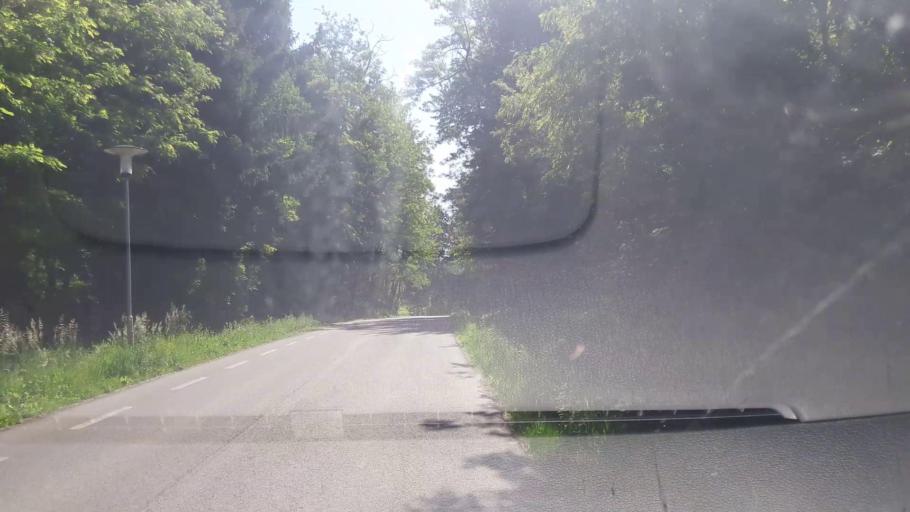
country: AT
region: Burgenland
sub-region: Politischer Bezirk Gussing
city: Stegersbach
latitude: 47.1707
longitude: 16.1417
